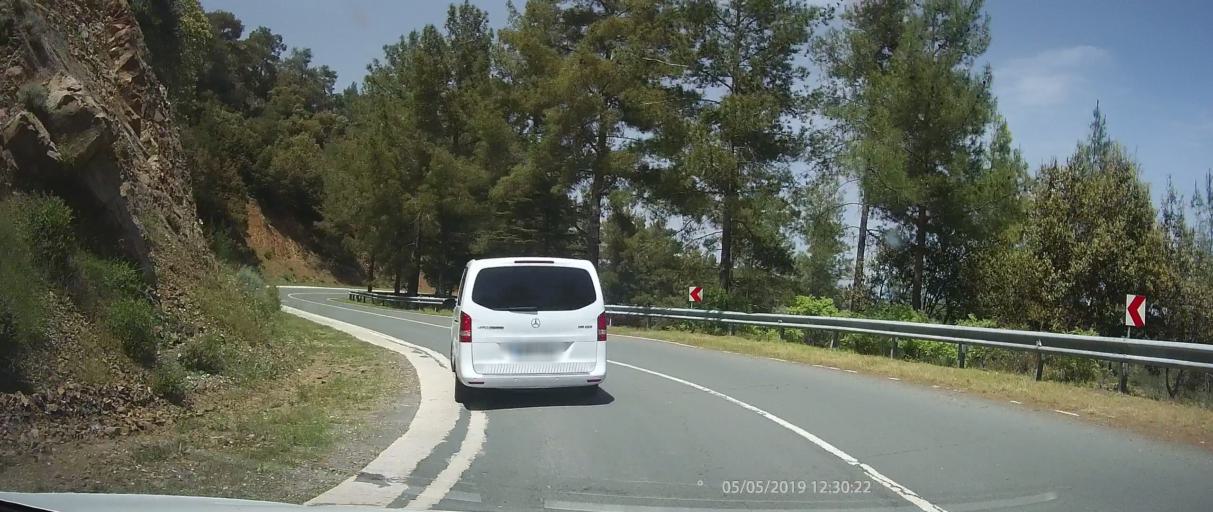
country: CY
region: Lefkosia
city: Kakopetria
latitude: 34.9836
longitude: 32.7493
